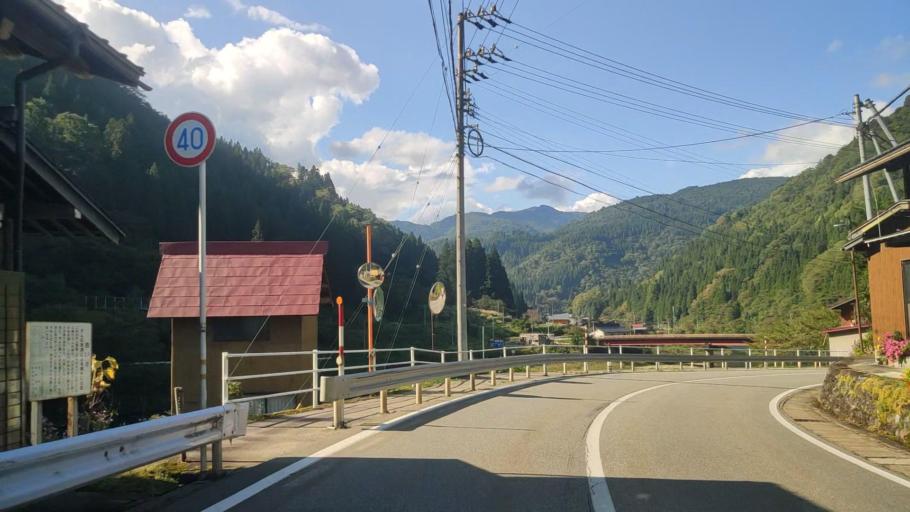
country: JP
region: Gifu
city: Takayama
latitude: 36.2964
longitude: 137.1157
